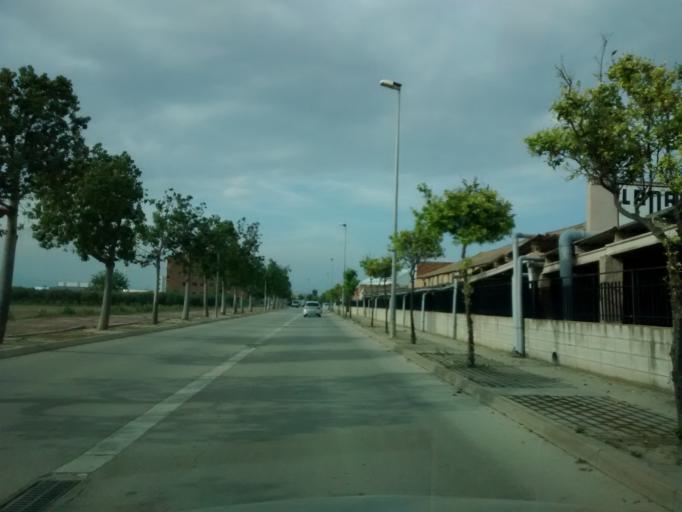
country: ES
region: Catalonia
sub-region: Provincia de Tarragona
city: Deltebre
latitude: 40.7196
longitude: 0.7211
